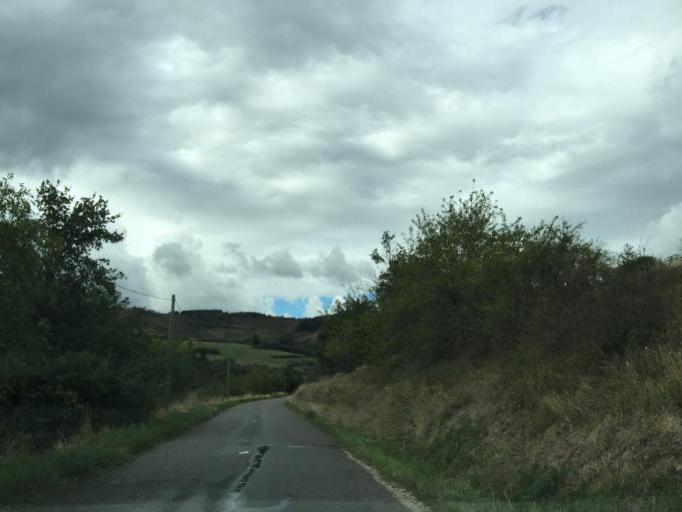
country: FR
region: Rhone-Alpes
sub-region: Departement de la Loire
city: Farnay
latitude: 45.4886
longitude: 4.6316
